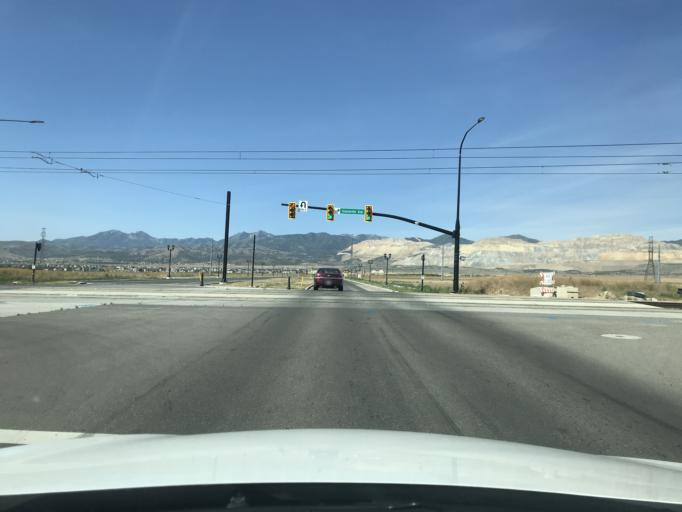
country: US
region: Utah
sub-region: Salt Lake County
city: Herriman
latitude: 40.5545
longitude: -112.0239
